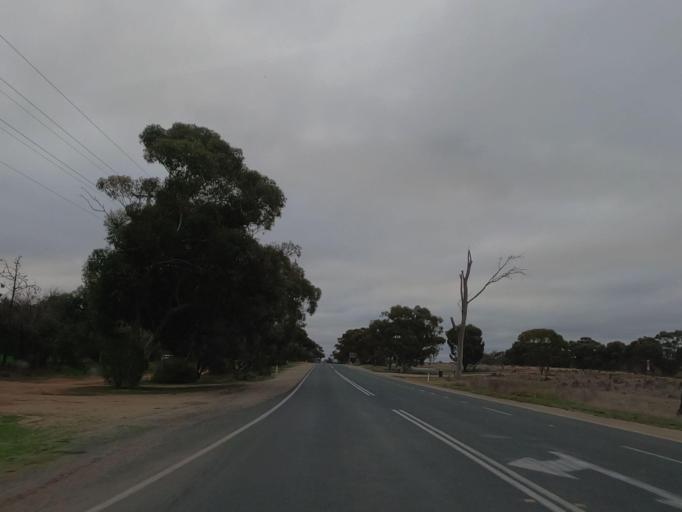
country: AU
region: Victoria
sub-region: Swan Hill
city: Swan Hill
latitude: -35.3851
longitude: 143.5668
